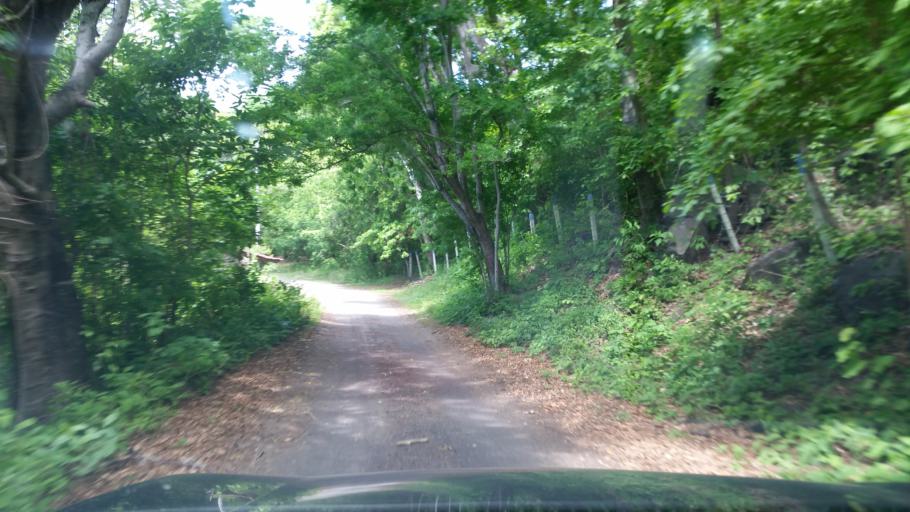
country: NI
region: Masaya
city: Catarina
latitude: 11.9158
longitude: -86.0584
